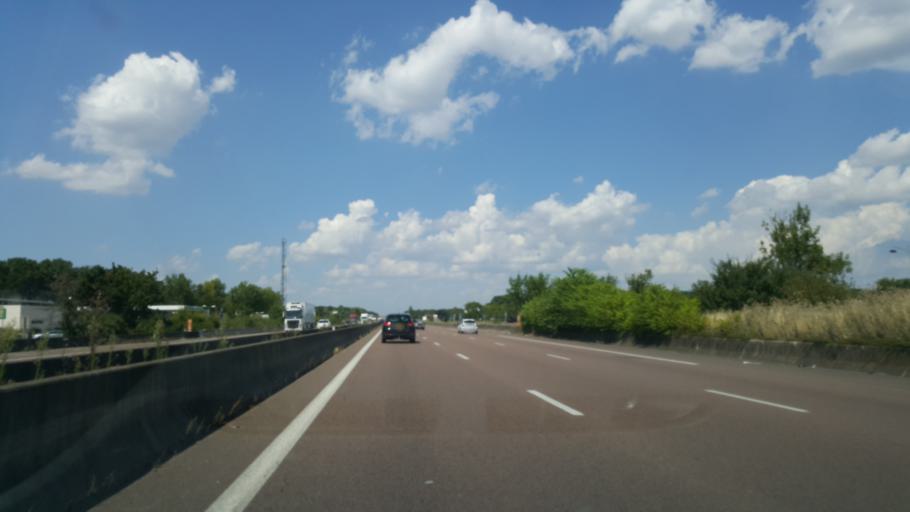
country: FR
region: Bourgogne
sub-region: Departement de Saone-et-Loire
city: Varennes-le-Grand
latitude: 46.6918
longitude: 4.8439
